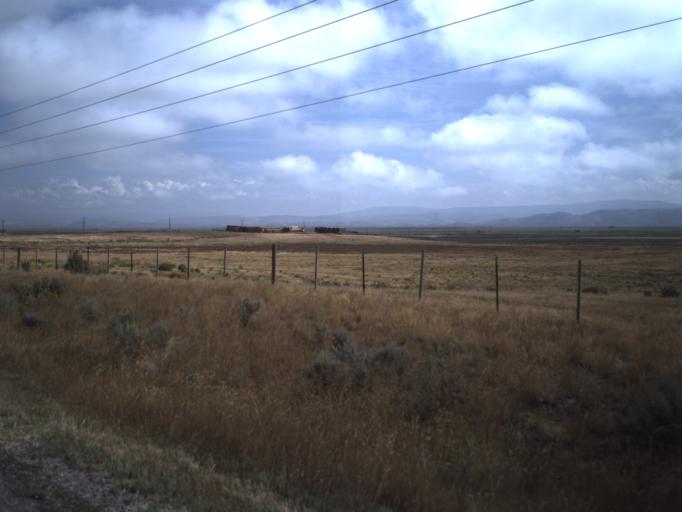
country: US
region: Utah
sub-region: Rich County
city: Randolph
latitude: 41.7457
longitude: -111.1493
